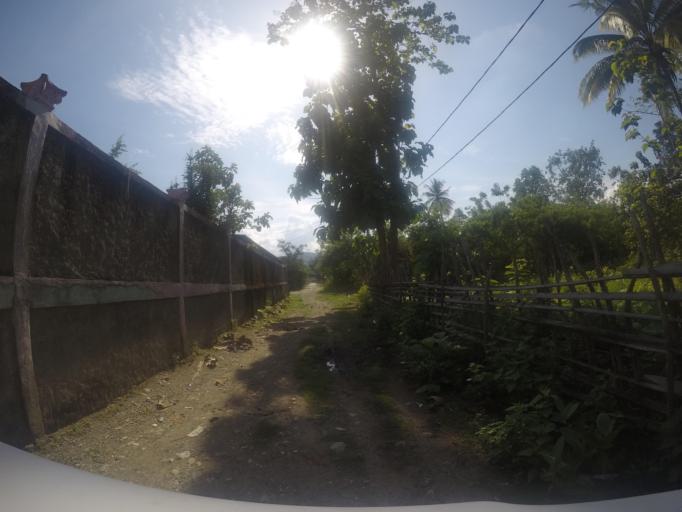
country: TL
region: Viqueque
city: Viqueque
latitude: -8.8562
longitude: 126.3610
